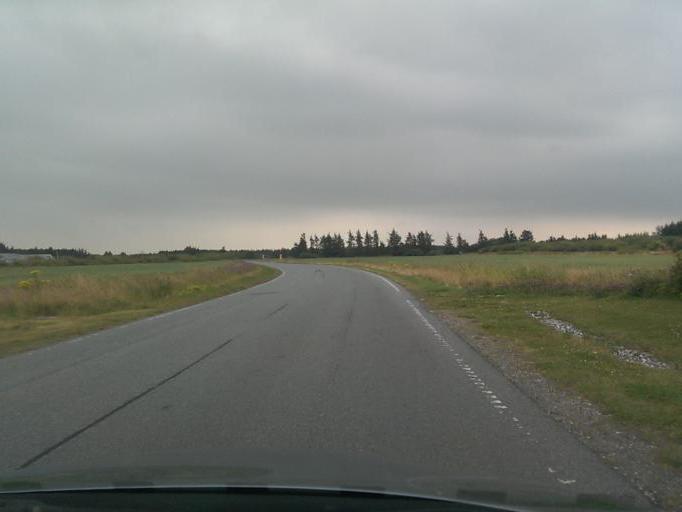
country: DK
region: North Denmark
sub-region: Jammerbugt Kommune
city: Pandrup
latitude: 57.3689
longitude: 9.7288
